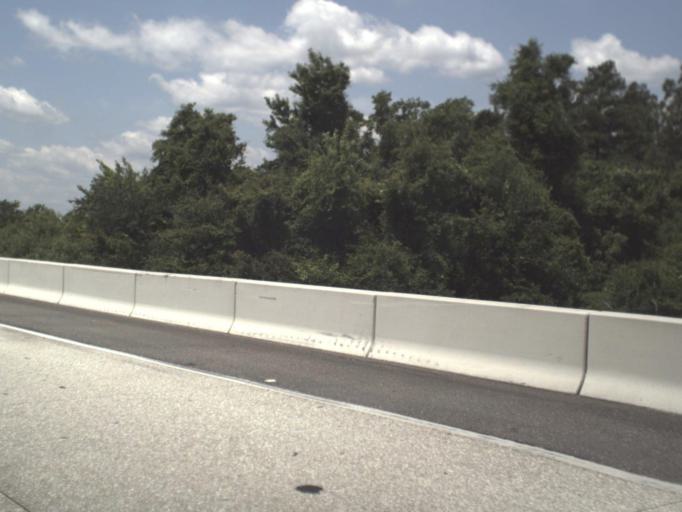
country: US
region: Florida
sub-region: Duval County
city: Jacksonville
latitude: 30.4032
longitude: -81.6617
